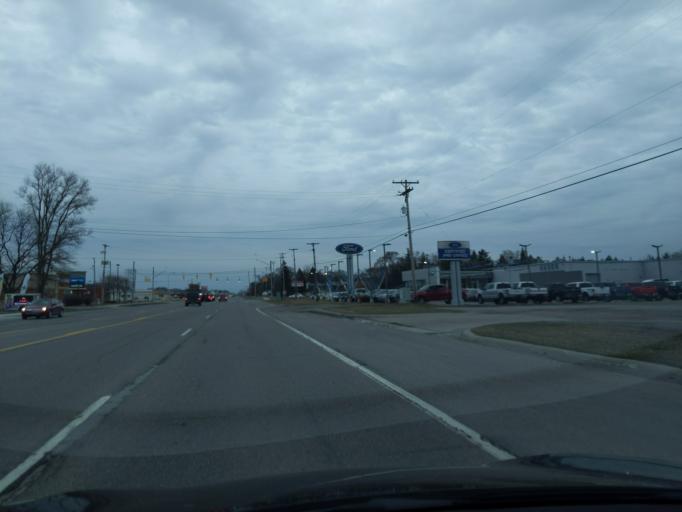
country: US
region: Michigan
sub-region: Bay County
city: Bay City
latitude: 43.6254
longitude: -83.9143
